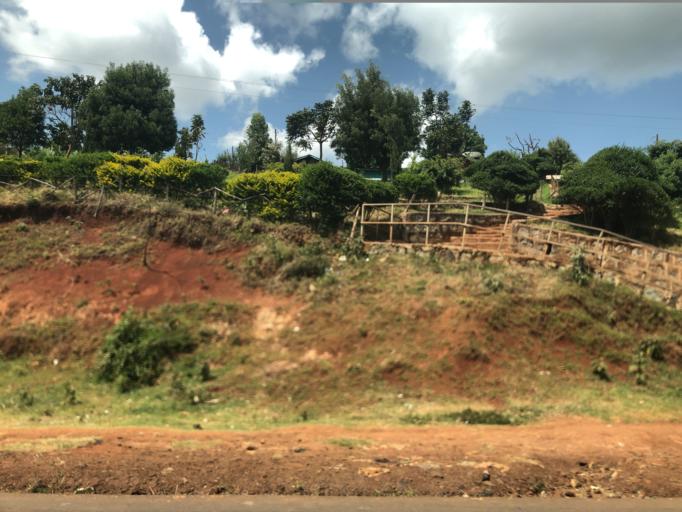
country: ET
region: Southern Nations, Nationalities, and People's Region
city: Boditi
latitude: 6.8715
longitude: 37.7690
